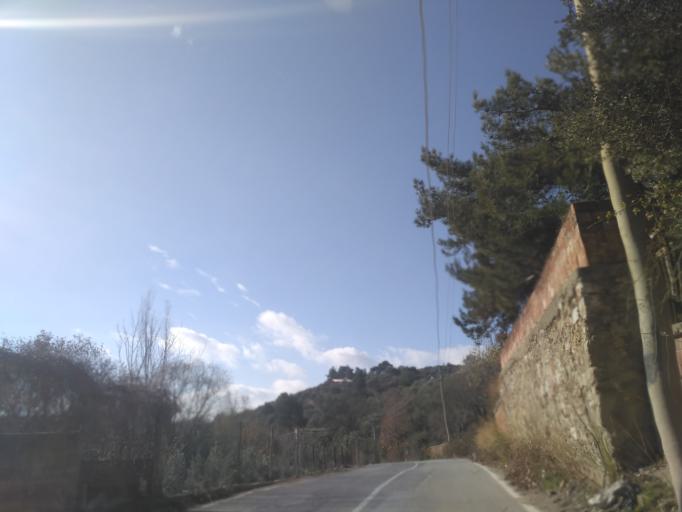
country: TR
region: Izmir
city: Buca
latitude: 38.3625
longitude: 27.2663
